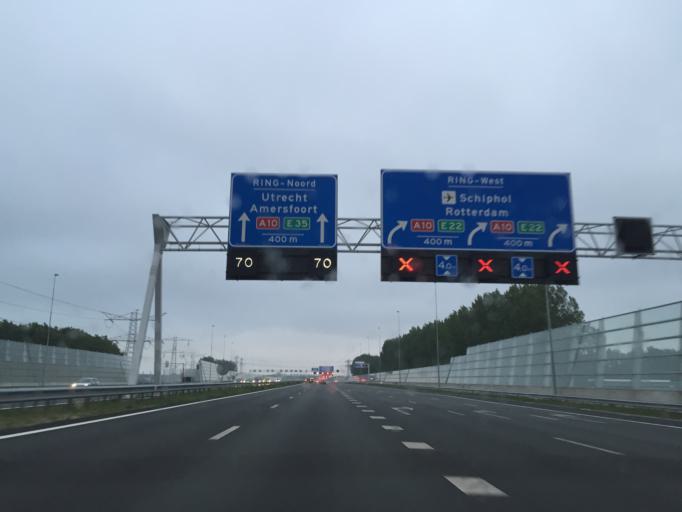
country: NL
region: North Holland
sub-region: Gemeente Zaanstad
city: Zaandam
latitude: 52.4348
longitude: 4.8644
